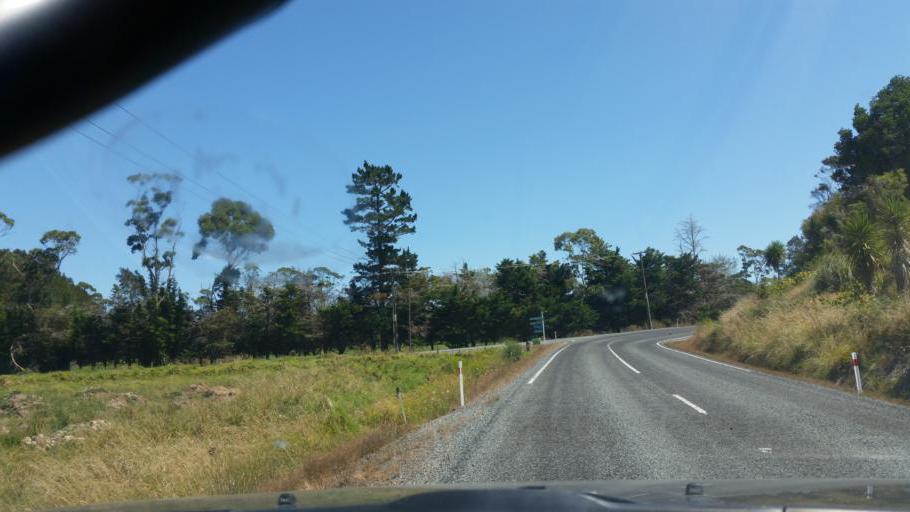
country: NZ
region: Northland
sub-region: Kaipara District
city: Dargaville
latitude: -36.0076
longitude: 173.9592
